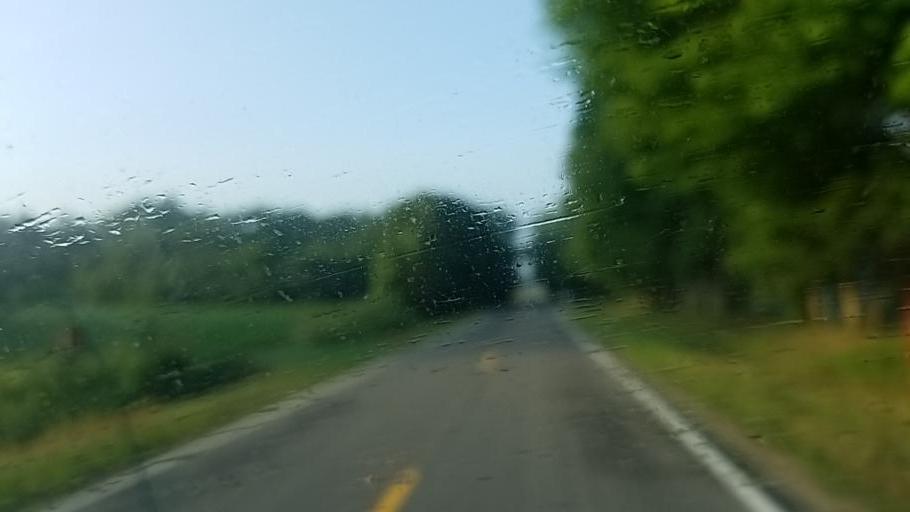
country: US
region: Michigan
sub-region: Muskegon County
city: Twin Lake
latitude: 43.4462
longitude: -86.0792
